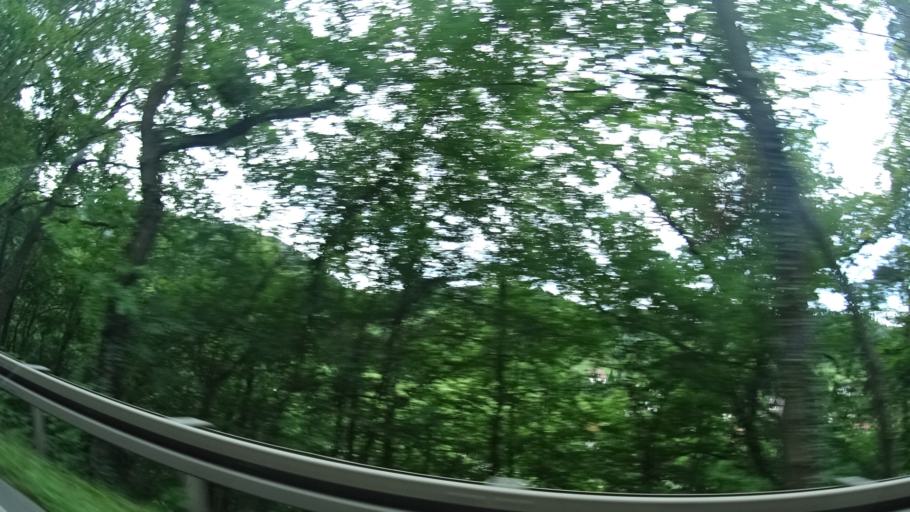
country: DE
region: Thuringia
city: Saalfeld
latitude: 50.6185
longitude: 11.3866
